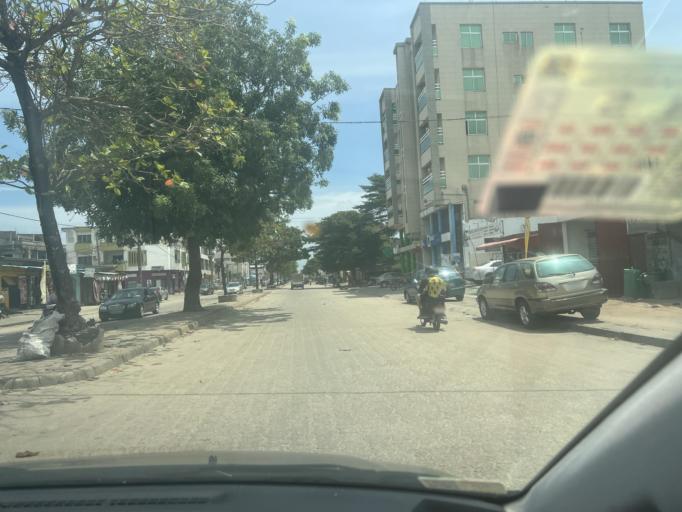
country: BJ
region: Littoral
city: Cotonou
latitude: 6.3818
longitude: 2.4470
